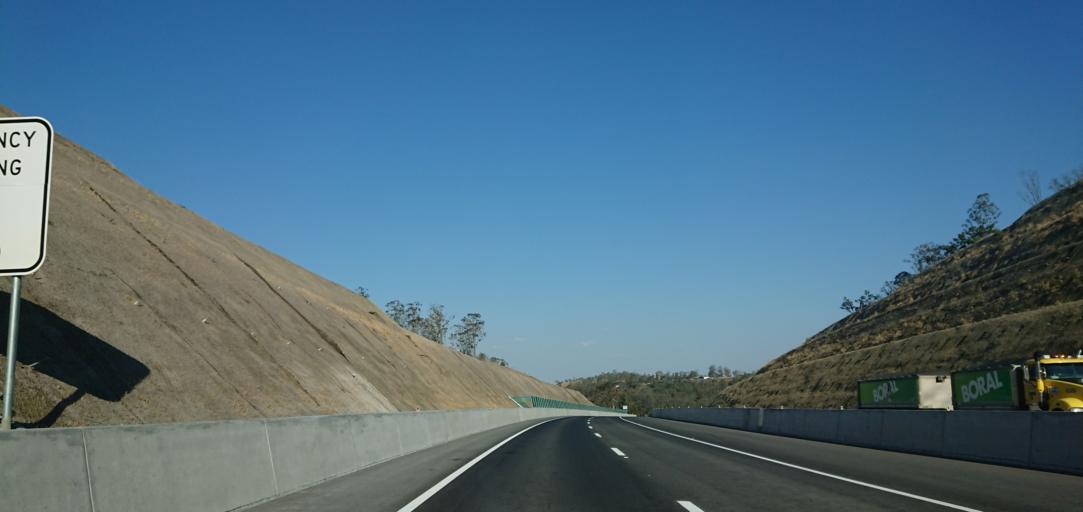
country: AU
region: Queensland
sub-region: Toowoomba
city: Toowoomba
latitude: -27.5016
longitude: 151.9918
